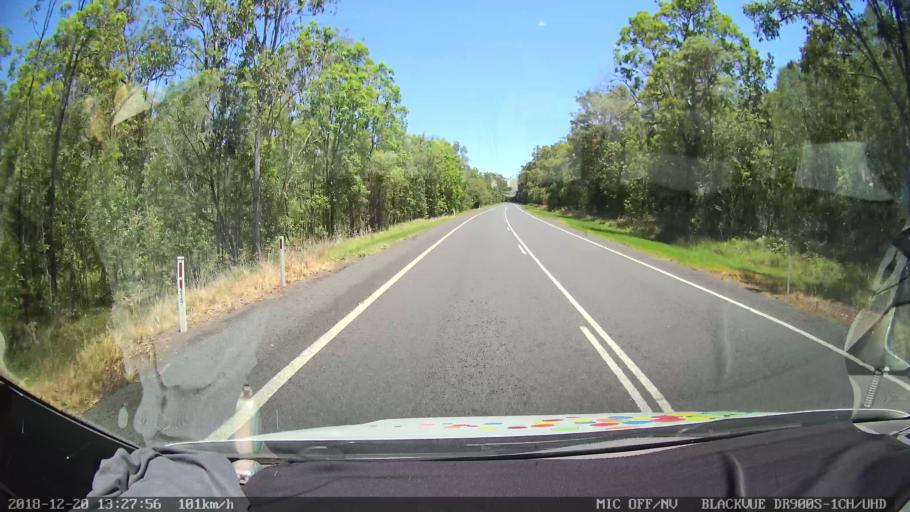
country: AU
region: New South Wales
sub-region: Clarence Valley
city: Gordon
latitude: -29.1675
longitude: 152.9929
